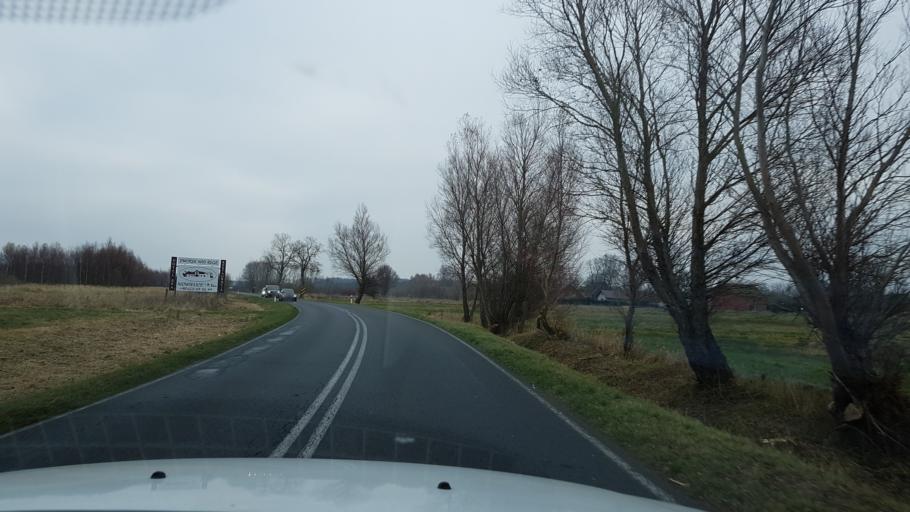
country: PL
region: West Pomeranian Voivodeship
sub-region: Powiat gryficki
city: Trzebiatow
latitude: 54.0707
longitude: 15.2298
